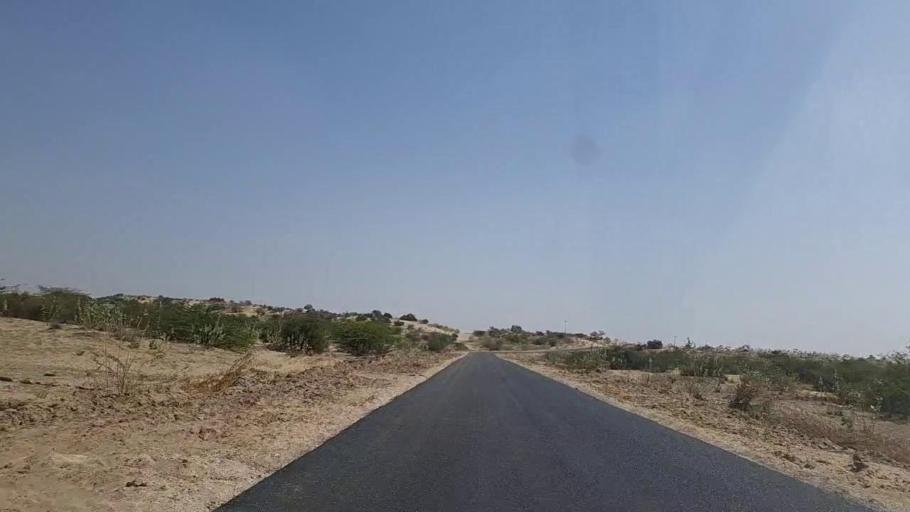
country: PK
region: Sindh
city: Diplo
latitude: 24.4808
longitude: 69.5256
